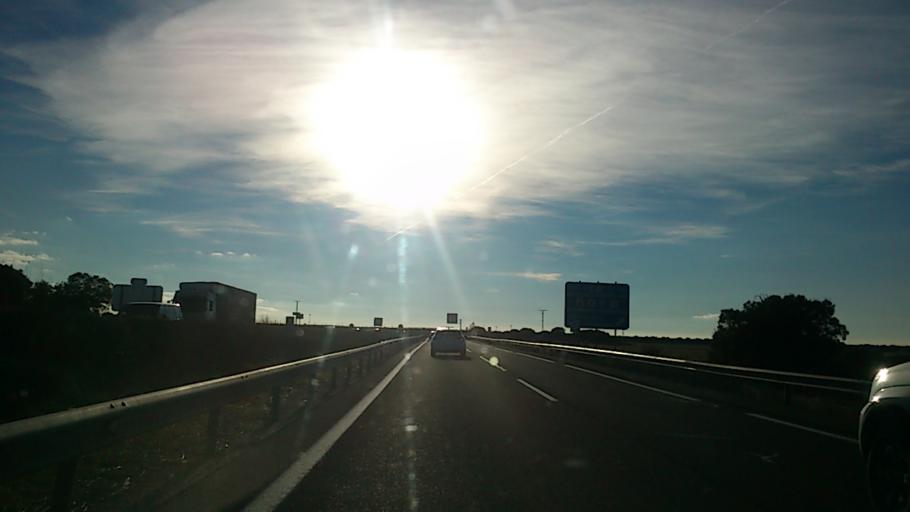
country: ES
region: Castille-La Mancha
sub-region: Provincia de Guadalajara
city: Mirabueno
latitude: 40.9354
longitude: -2.7068
